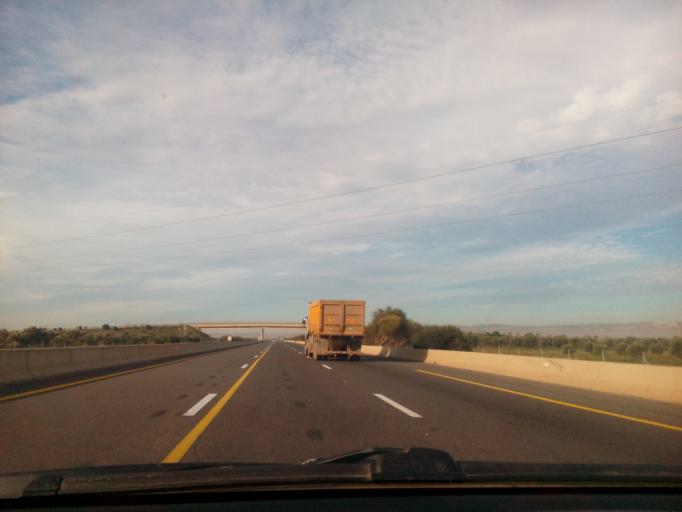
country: DZ
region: Mascara
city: Sig
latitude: 35.5812
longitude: -0.2368
